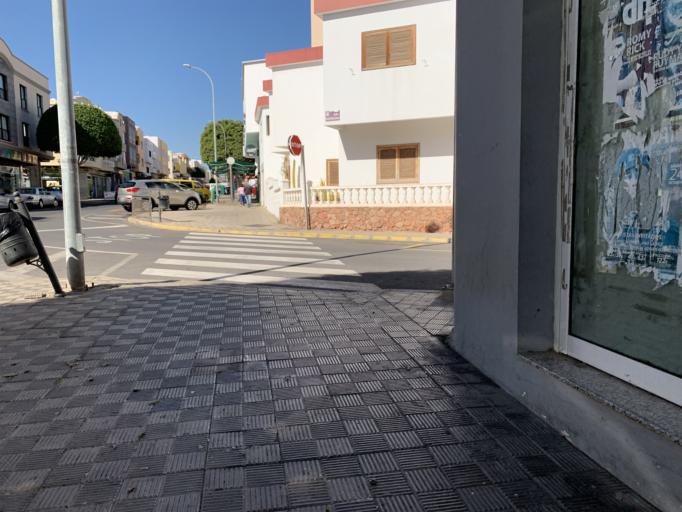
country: ES
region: Canary Islands
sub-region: Provincia de Las Palmas
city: Puerto del Rosario
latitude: 28.5019
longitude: -13.8696
